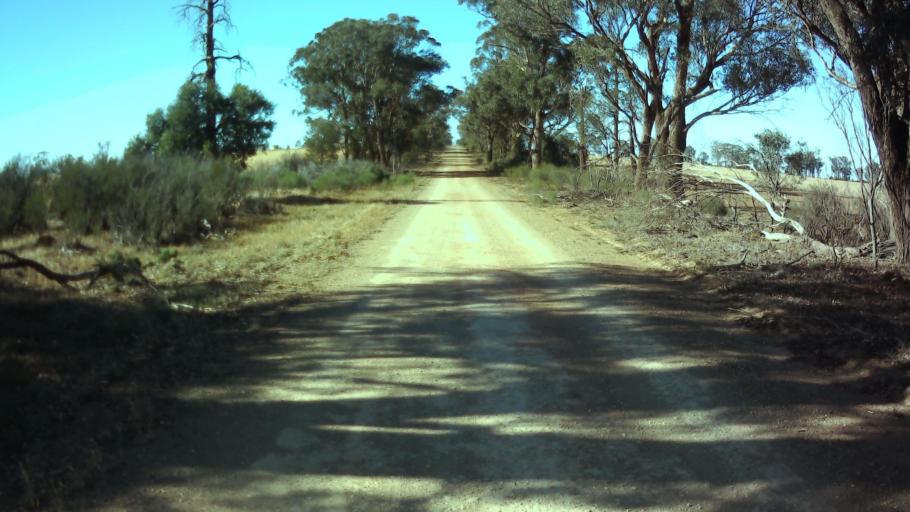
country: AU
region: New South Wales
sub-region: Weddin
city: Grenfell
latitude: -33.8967
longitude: 147.8794
